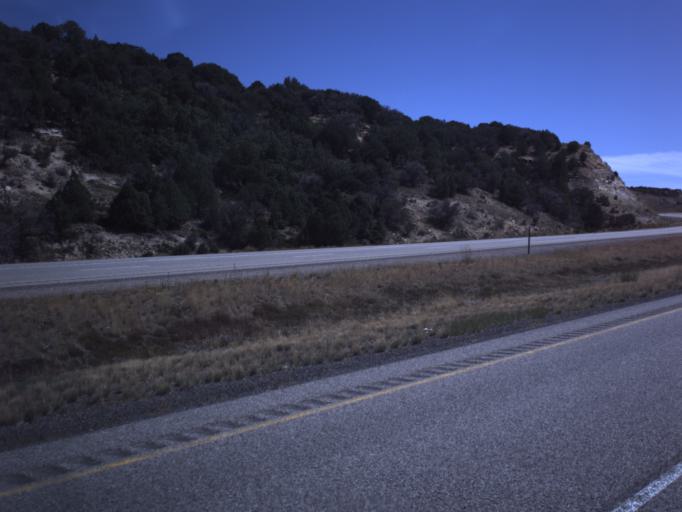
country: US
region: Utah
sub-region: Sevier County
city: Salina
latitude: 38.7849
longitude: -111.4972
